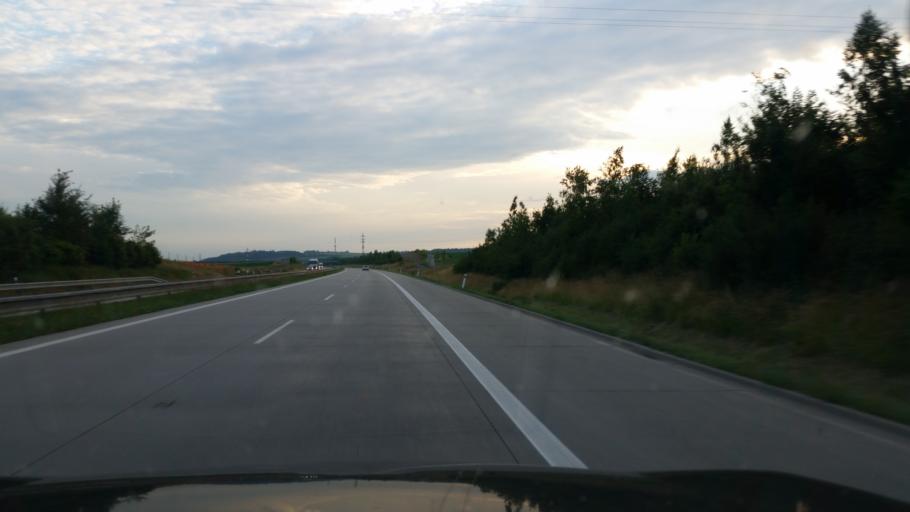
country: CZ
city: Studenka
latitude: 49.7405
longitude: 18.0519
